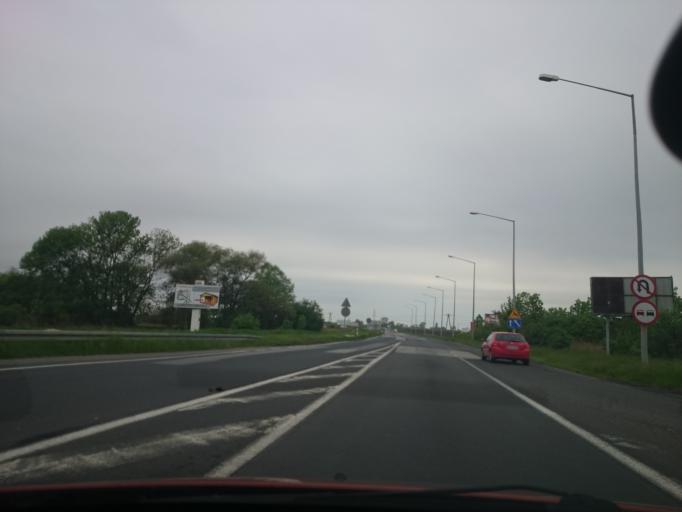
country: PL
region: Opole Voivodeship
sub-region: Powiat opolski
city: Opole
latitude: 50.7041
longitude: 17.9319
